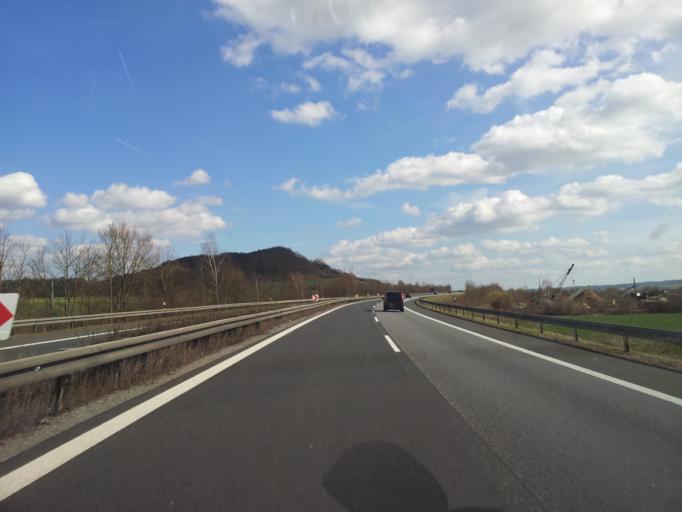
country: DE
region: Bavaria
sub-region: Regierungsbezirk Unterfranken
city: Stettfeld
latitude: 49.9653
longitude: 10.7231
